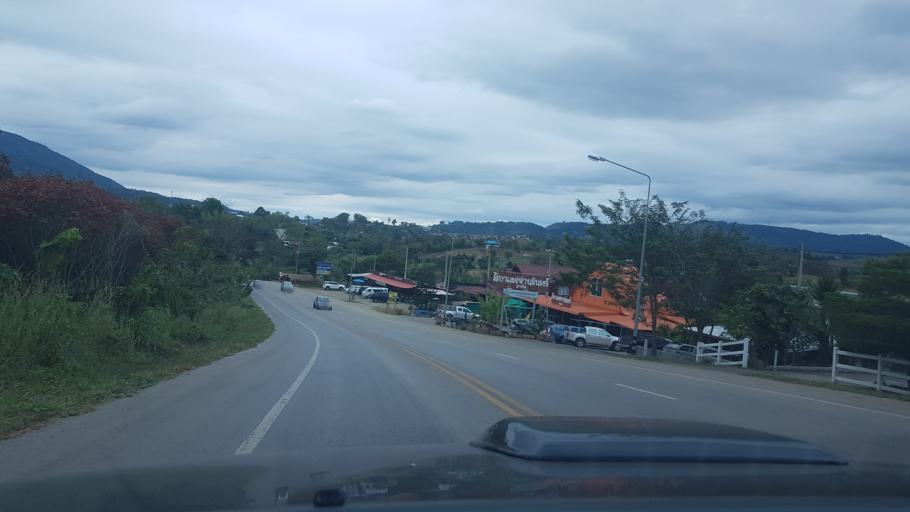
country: TH
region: Phetchabun
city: Khao Kho
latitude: 16.5593
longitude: 101.0238
